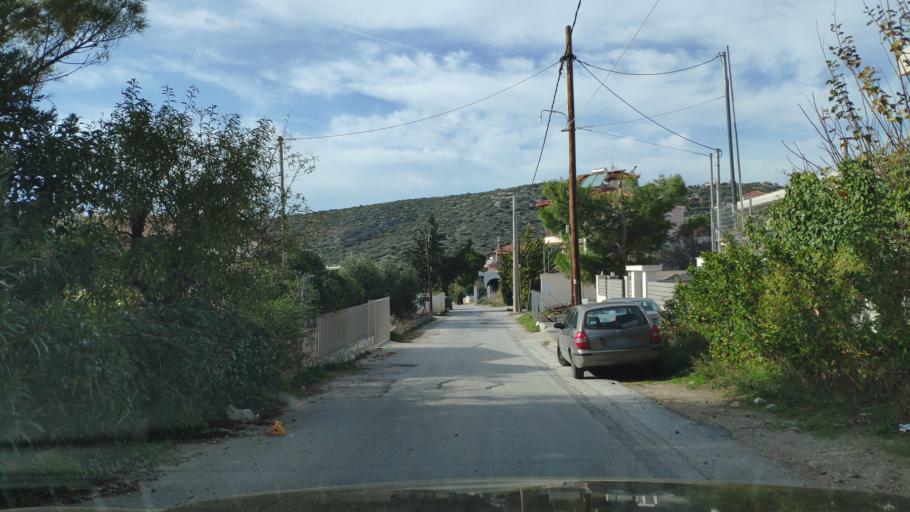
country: GR
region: Attica
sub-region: Nomarchia Anatolikis Attikis
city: Limin Mesoyaias
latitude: 37.8998
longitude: 24.0260
